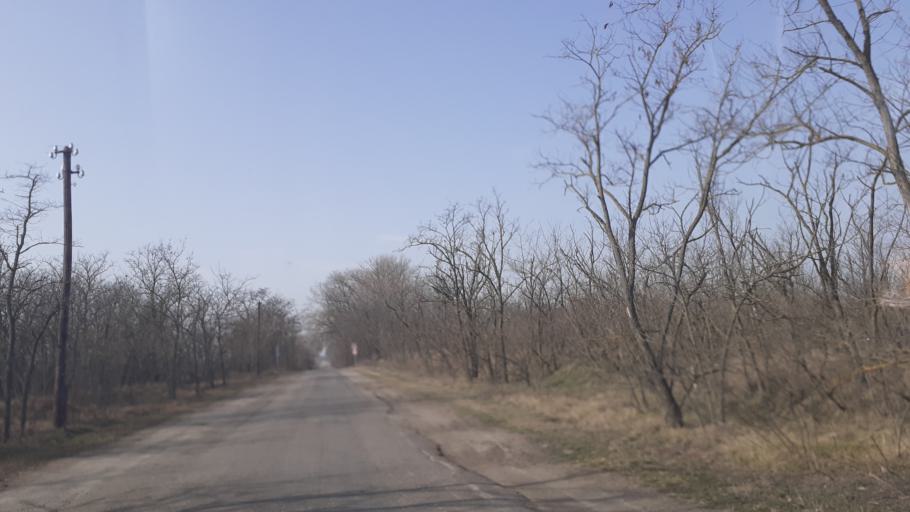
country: HU
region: Pest
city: Dabas
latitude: 47.0659
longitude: 19.2707
